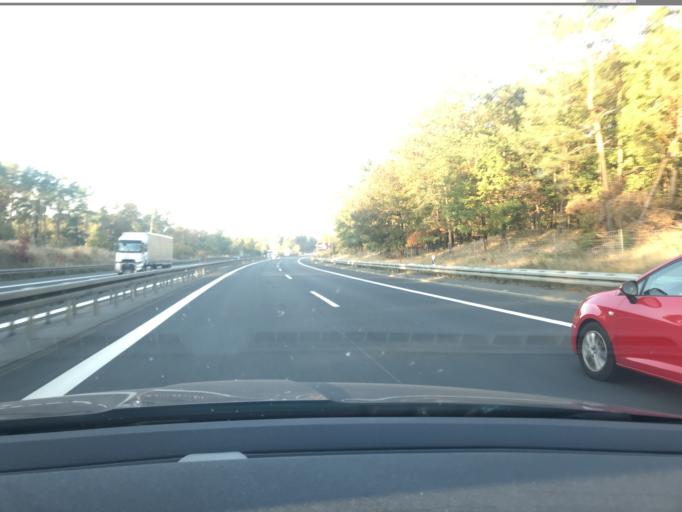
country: DE
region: Saxony
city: Thiendorf
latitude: 51.2590
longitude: 13.7225
